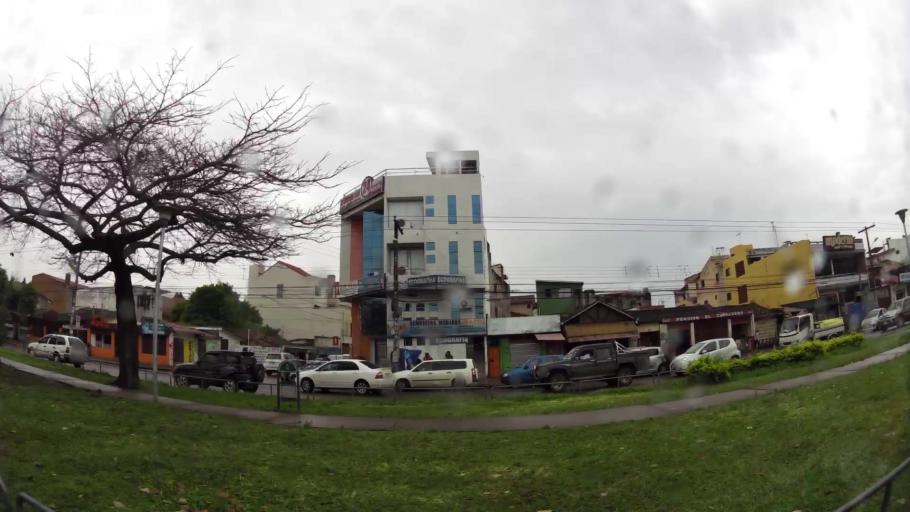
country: BO
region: Santa Cruz
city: Santa Cruz de la Sierra
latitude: -17.7877
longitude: -63.1881
